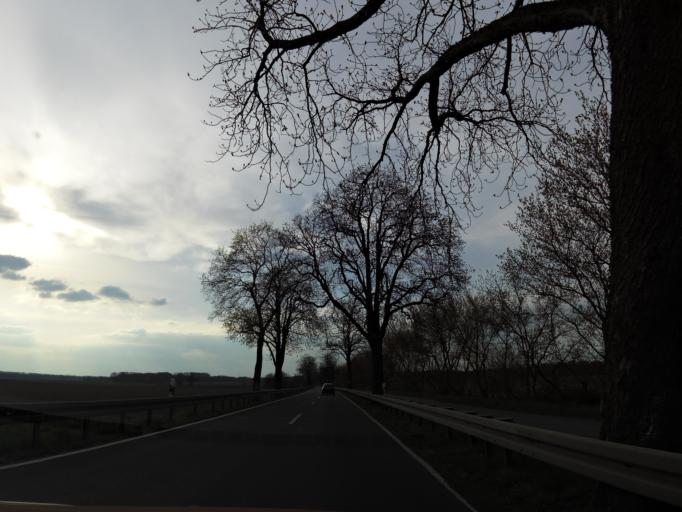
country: DE
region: Brandenburg
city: Rangsdorf
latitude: 52.3341
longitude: 13.3876
